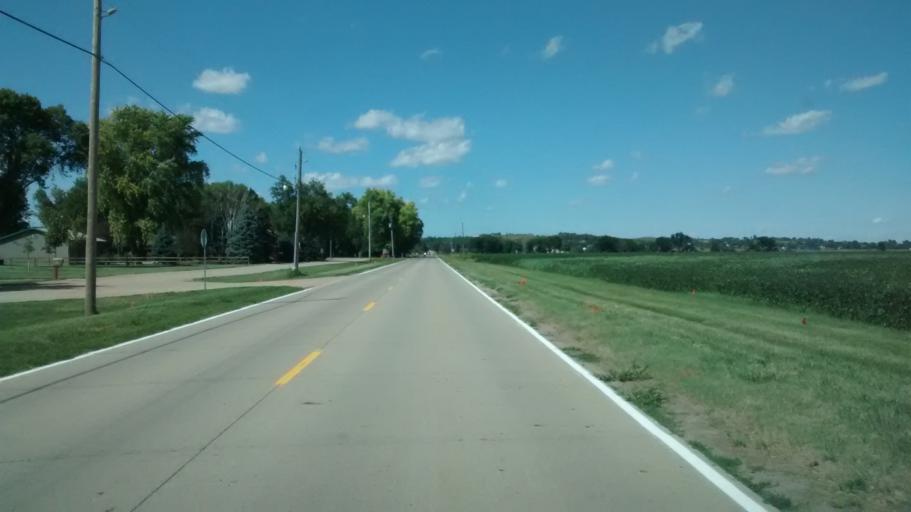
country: US
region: Iowa
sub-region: Woodbury County
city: Sergeant Bluff
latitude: 42.3915
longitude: -96.3407
